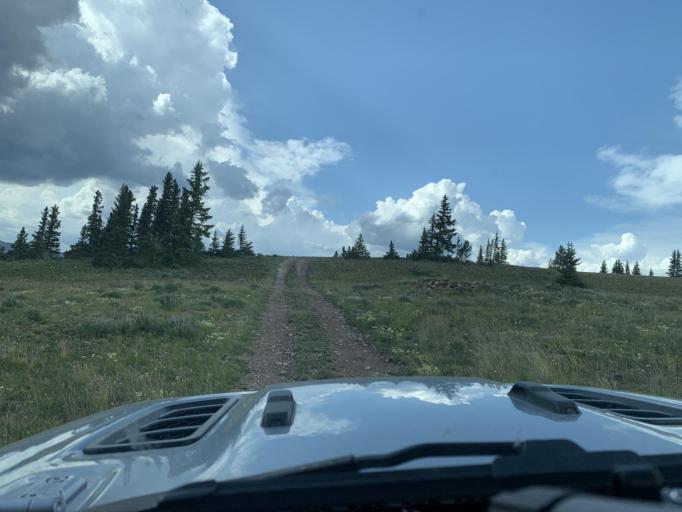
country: US
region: Colorado
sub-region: Lake County
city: Leadville North
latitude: 39.3085
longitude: -106.2897
